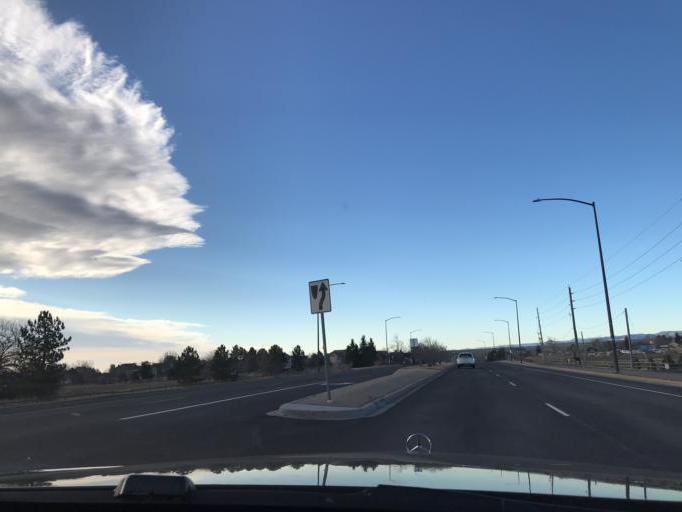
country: US
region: Colorado
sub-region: Boulder County
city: Superior
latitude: 39.9802
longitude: -105.1660
